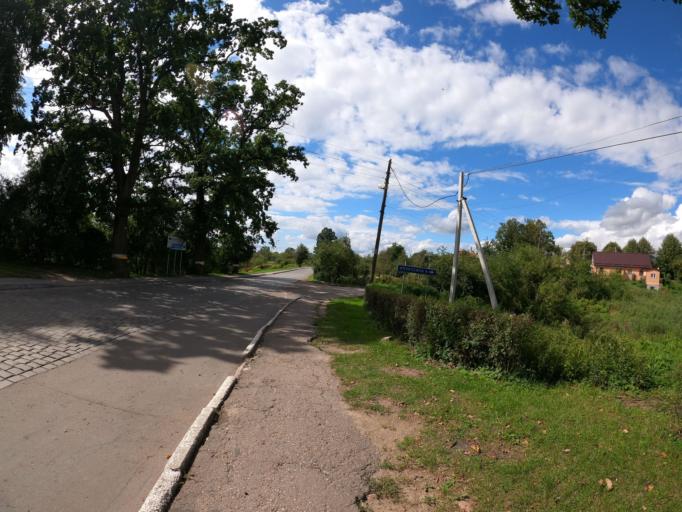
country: RU
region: Kaliningrad
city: Zheleznodorozhnyy
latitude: 54.3618
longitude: 21.3030
